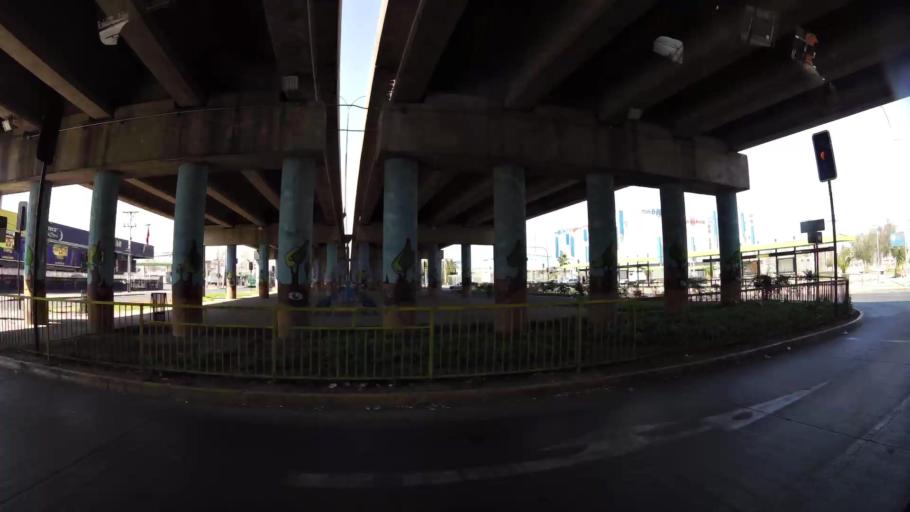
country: CL
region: Santiago Metropolitan
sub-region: Provincia de Santiago
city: Lo Prado
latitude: -33.4025
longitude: -70.6823
